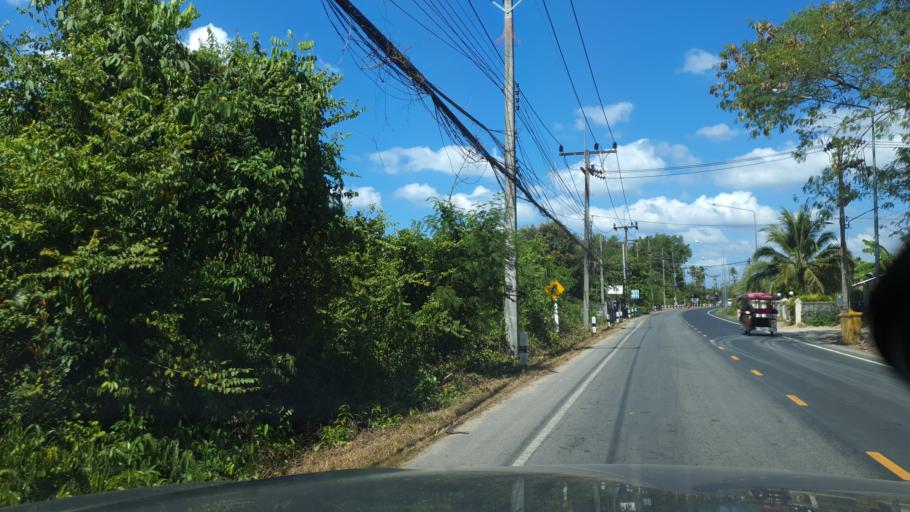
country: TH
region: Phuket
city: Thalang
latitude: 8.1380
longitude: 98.3065
